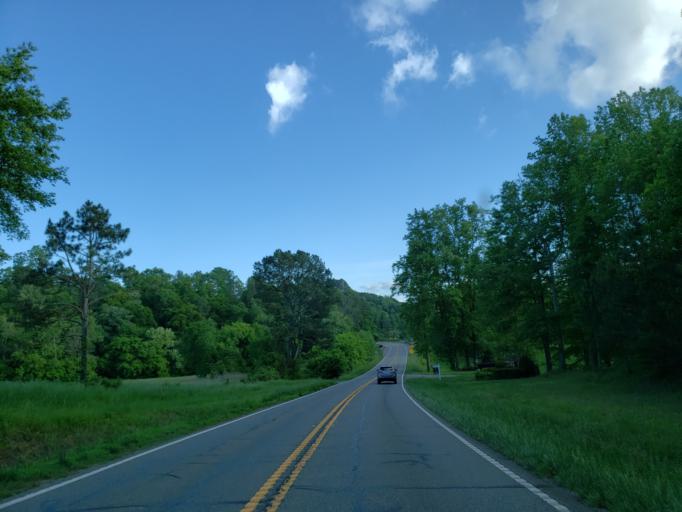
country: US
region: Georgia
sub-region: Cherokee County
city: Canton
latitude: 34.3286
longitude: -84.5616
